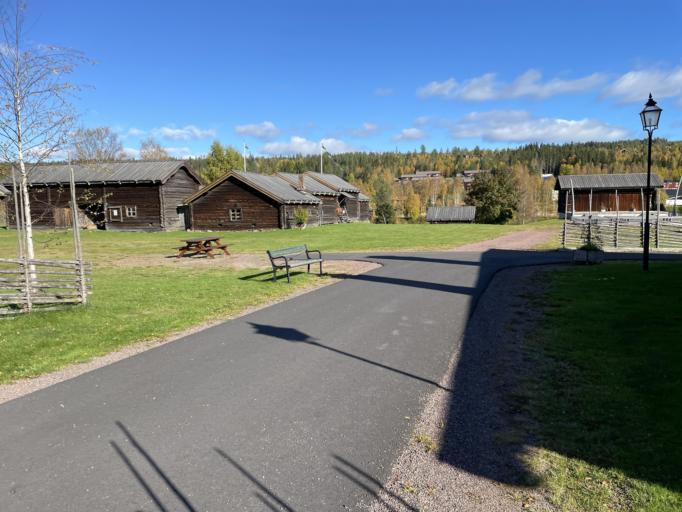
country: SE
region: Dalarna
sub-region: Malung-Saelens kommun
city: Malung
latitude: 61.1585
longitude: 13.2577
